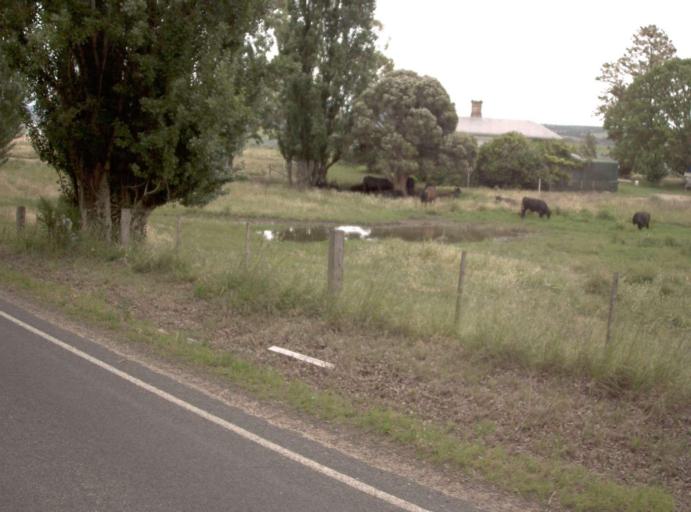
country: AU
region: Victoria
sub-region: East Gippsland
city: Bairnsdale
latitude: -37.7995
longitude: 147.4519
